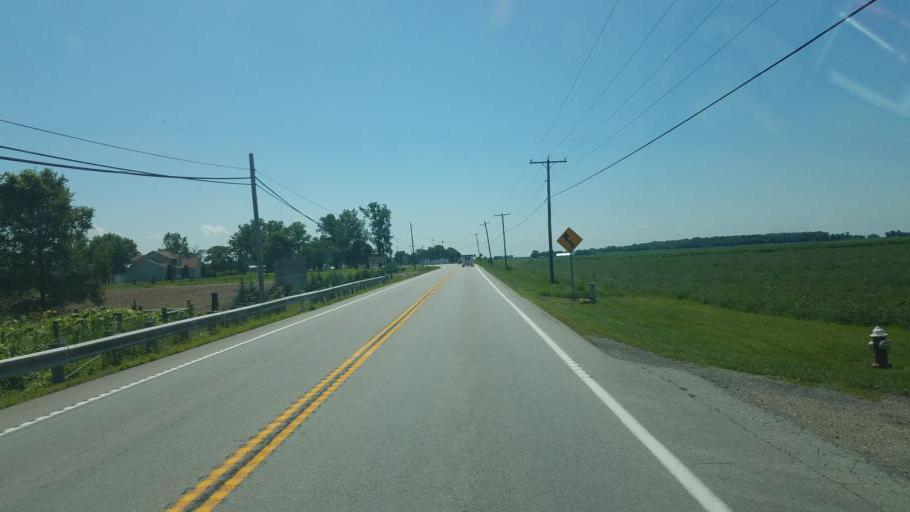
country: US
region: Ohio
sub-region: Erie County
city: Sandusky
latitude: 41.4415
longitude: -82.8139
